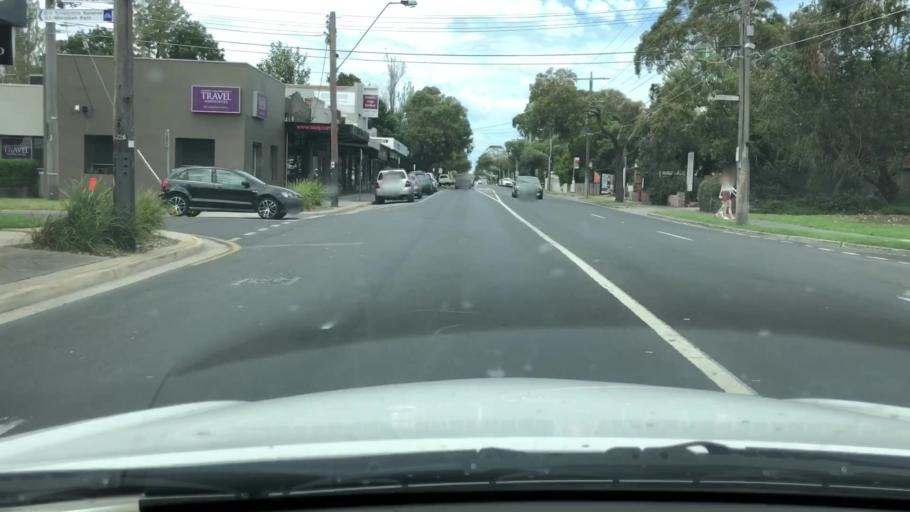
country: AU
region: Victoria
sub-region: Bayside
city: Black Rock
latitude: -37.9593
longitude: 145.0195
